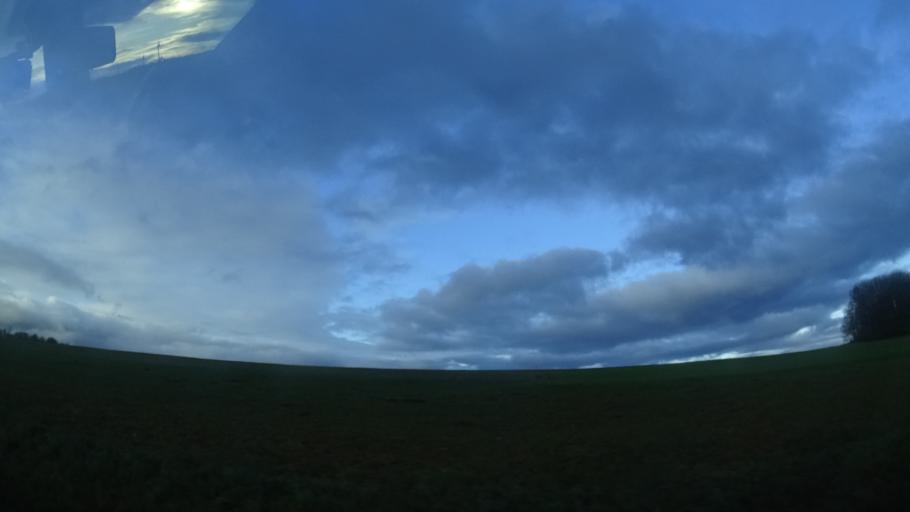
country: DE
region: Hesse
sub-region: Regierungsbezirk Giessen
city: Freiensteinau
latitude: 50.4570
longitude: 9.4361
